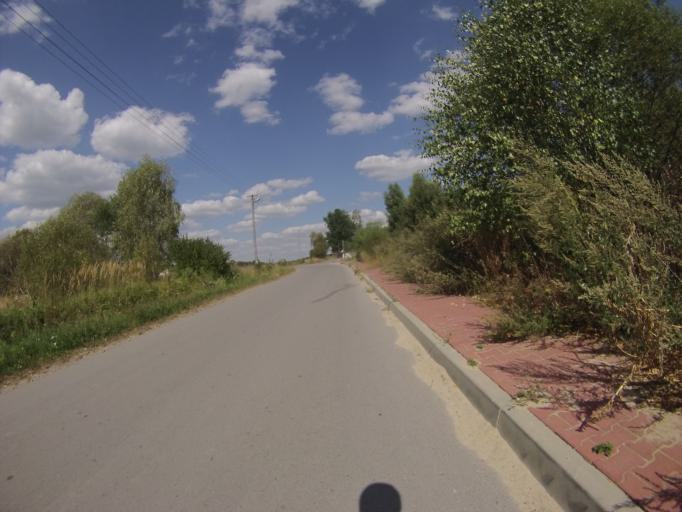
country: PL
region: Swietokrzyskie
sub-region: Powiat kielecki
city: Rakow
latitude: 50.7038
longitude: 21.0541
